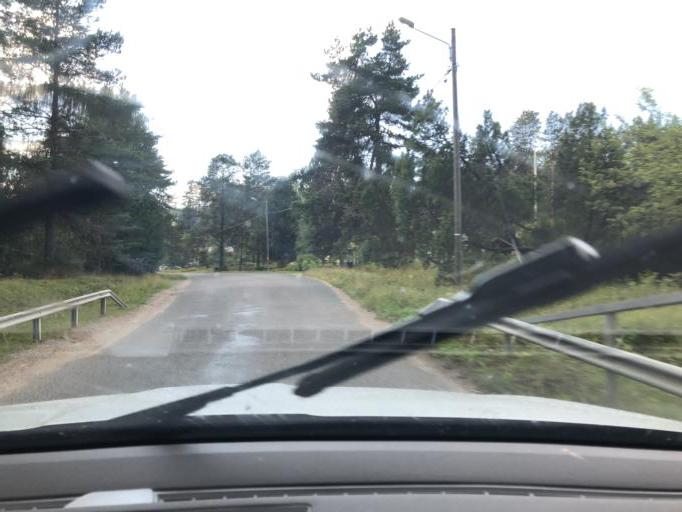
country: SE
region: Vaesternorrland
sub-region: Solleftea Kommun
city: Solleftea
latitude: 63.2476
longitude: 17.1956
